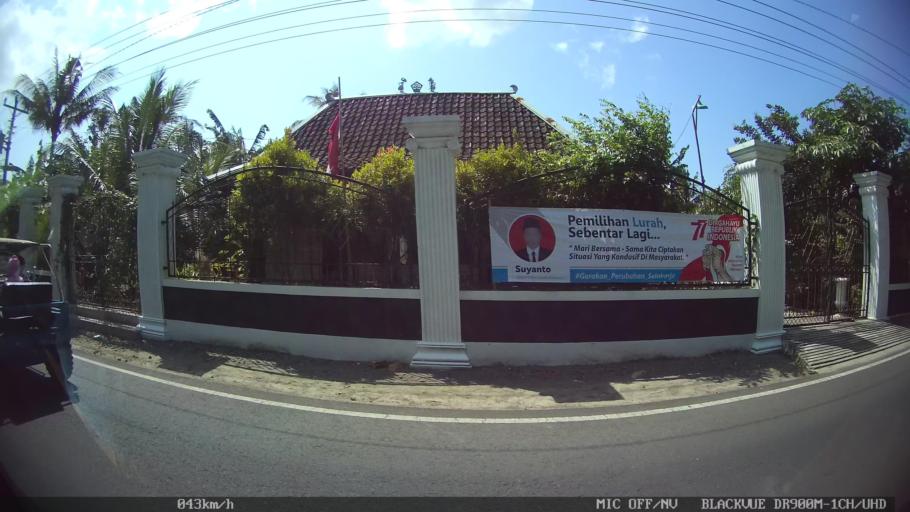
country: ID
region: Daerah Istimewa Yogyakarta
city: Pundong
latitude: -7.9870
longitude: 110.3302
